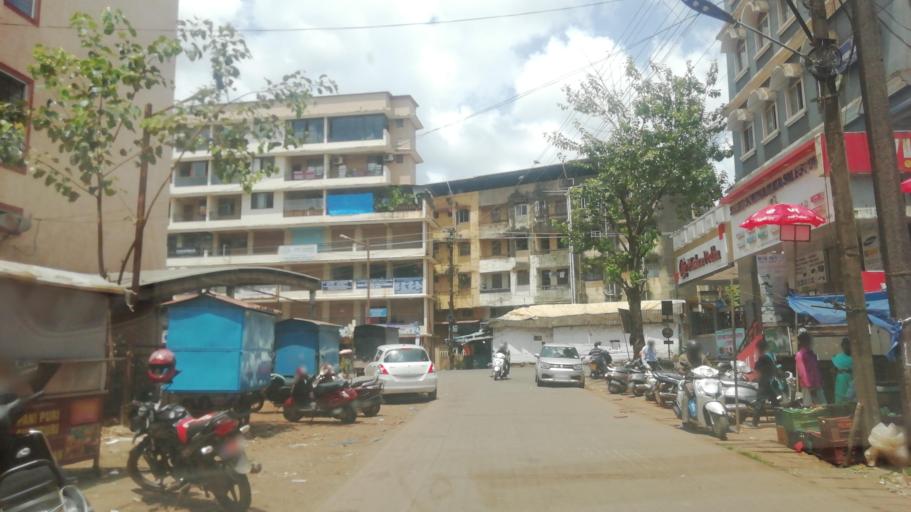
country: IN
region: Goa
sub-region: North Goa
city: Ponda
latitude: 15.4021
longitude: 74.0100
